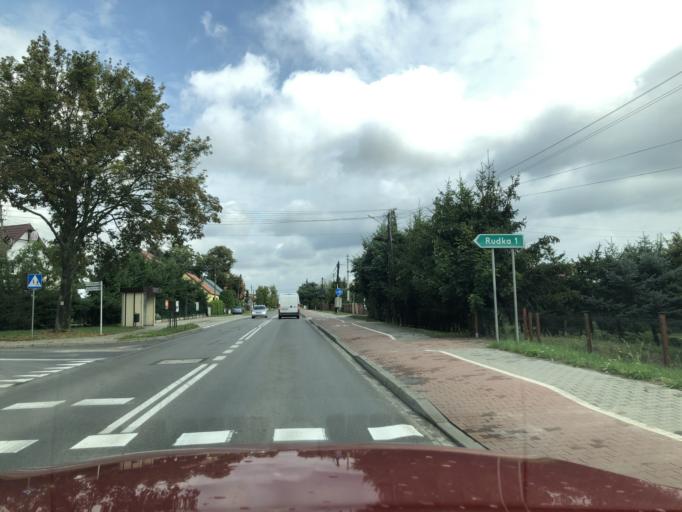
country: PL
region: Greater Poland Voivodeship
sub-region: Powiat szamotulski
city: Pniewy
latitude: 52.5197
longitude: 16.2644
